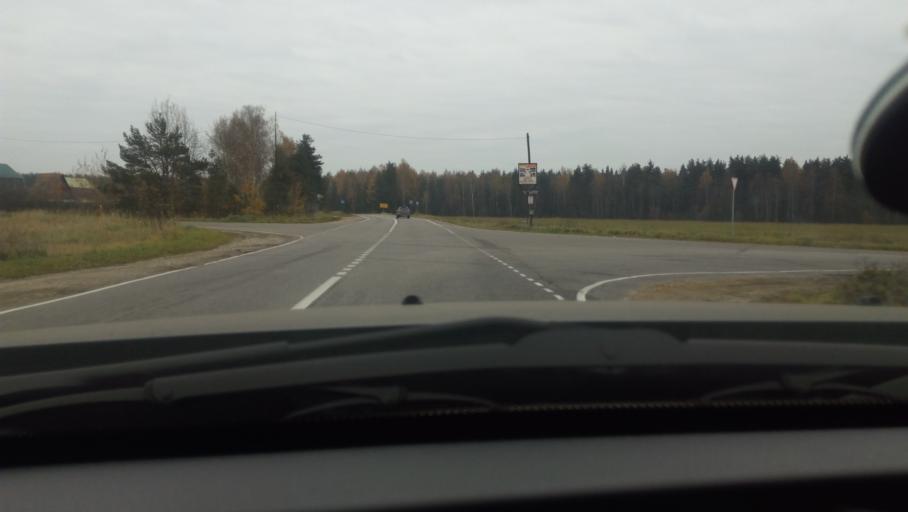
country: RU
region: Moskovskaya
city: Drezna
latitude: 55.7059
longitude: 38.8681
